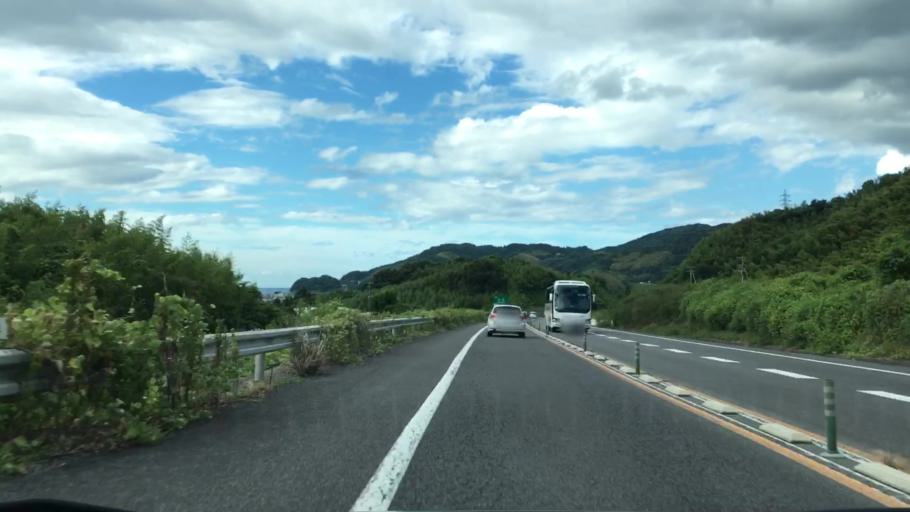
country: JP
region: Saga Prefecture
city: Karatsu
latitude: 33.4355
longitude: 130.0480
